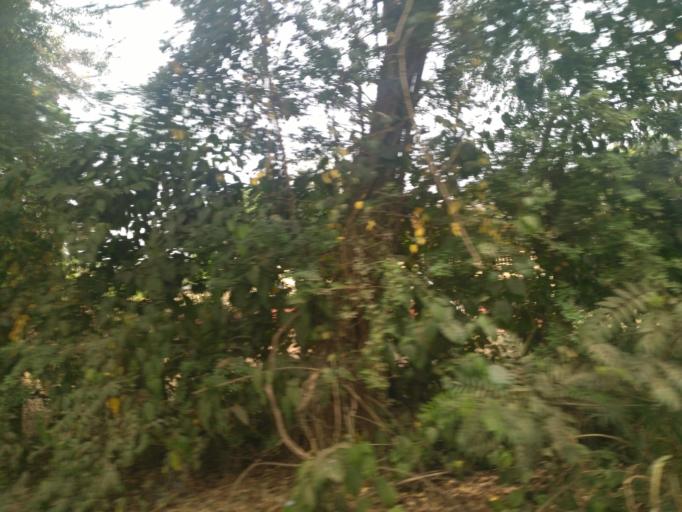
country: GH
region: Ashanti
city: Kumasi
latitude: 6.6843
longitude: -1.6328
